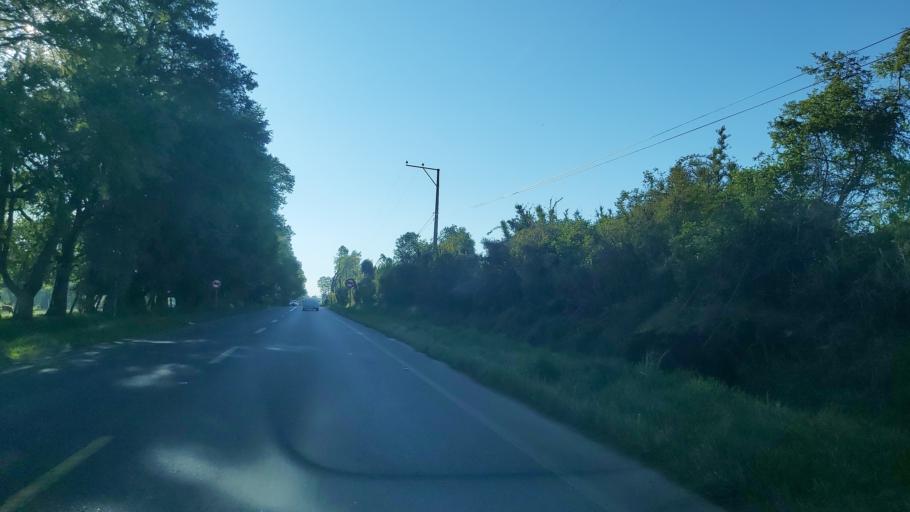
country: CL
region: Araucania
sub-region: Provincia de Malleco
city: Victoria
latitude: -38.2688
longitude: -72.2151
